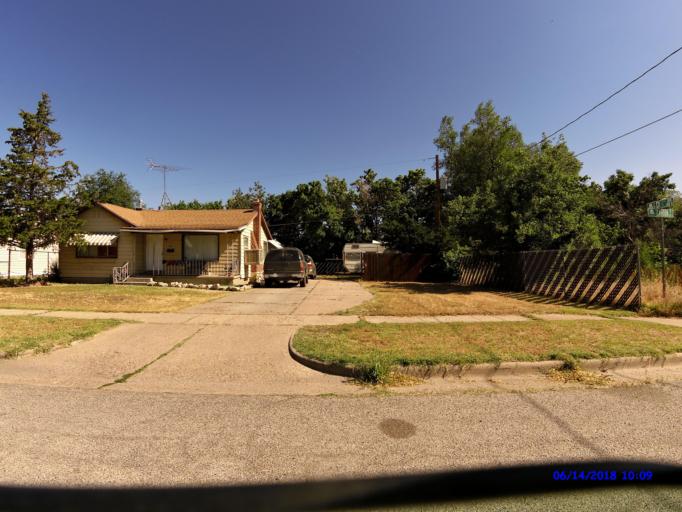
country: US
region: Utah
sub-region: Weber County
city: Ogden
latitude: 41.2241
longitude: -111.9943
